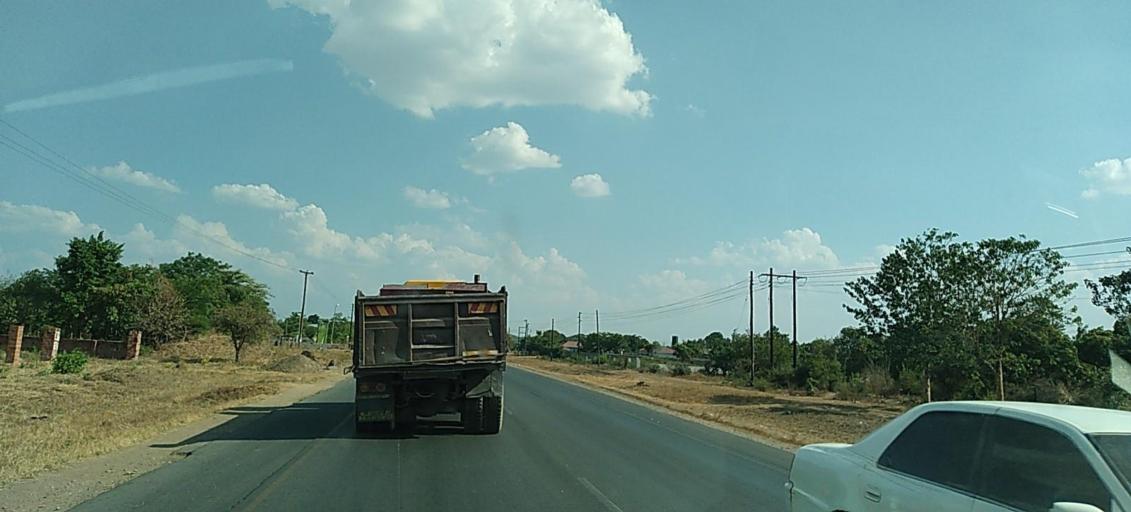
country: ZM
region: Lusaka
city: Lusaka
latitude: -15.2357
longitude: 28.2566
